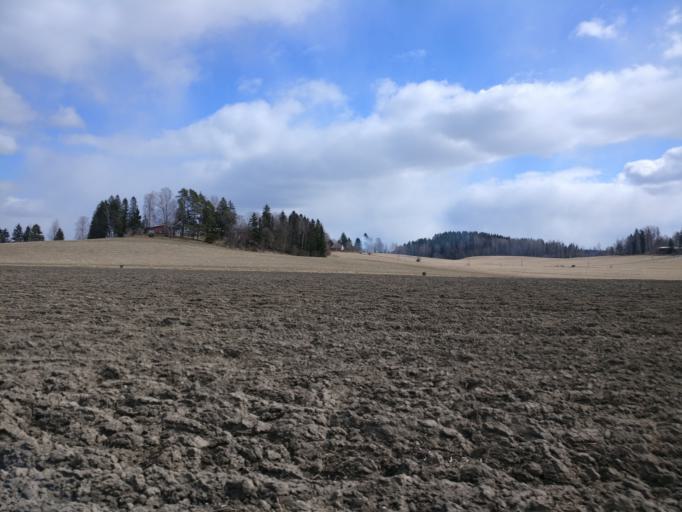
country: FI
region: Uusimaa
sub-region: Helsinki
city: Karjalohja
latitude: 60.2449
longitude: 23.7380
